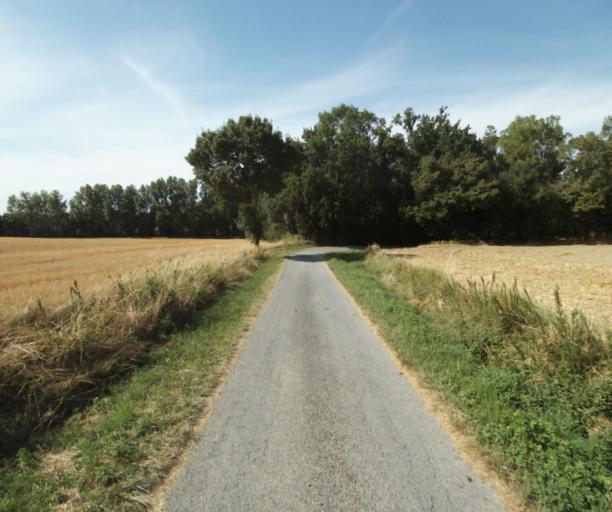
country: FR
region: Midi-Pyrenees
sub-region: Departement du Tarn
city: Soreze
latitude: 43.5132
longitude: 2.0551
